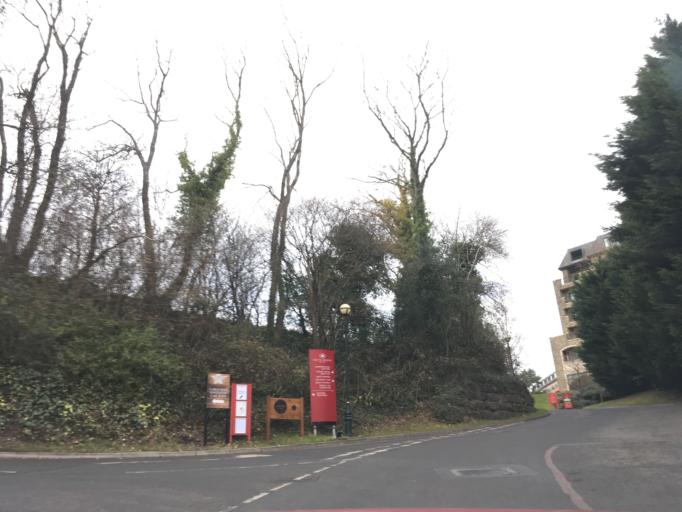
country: GB
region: Wales
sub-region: Newport
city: Langstone
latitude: 51.6016
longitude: -2.9330
